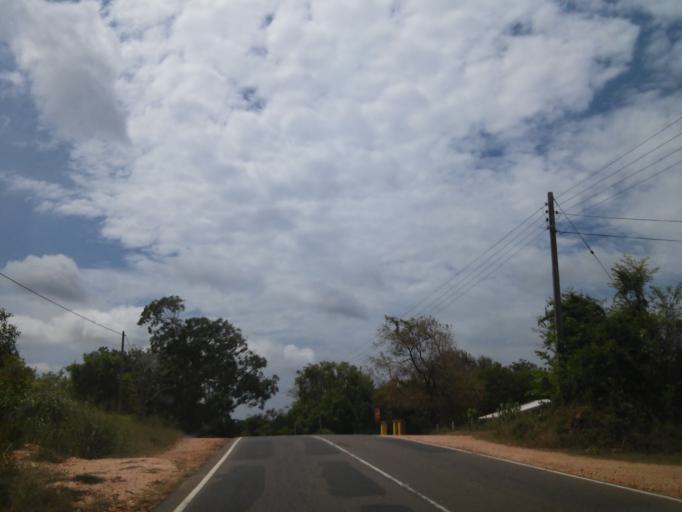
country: LK
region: Central
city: Sigiriya
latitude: 8.0679
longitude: 80.6984
